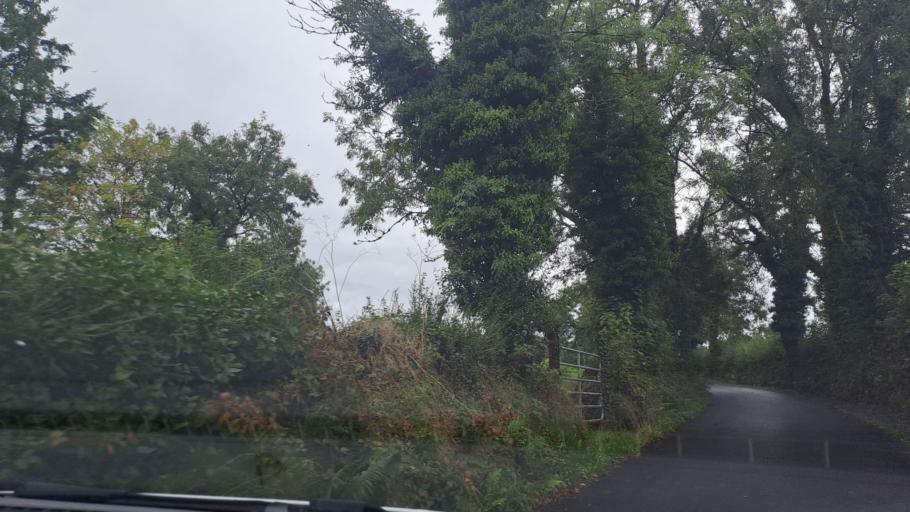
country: IE
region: Ulster
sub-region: An Cabhan
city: Kingscourt
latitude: 53.9816
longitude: -6.8122
